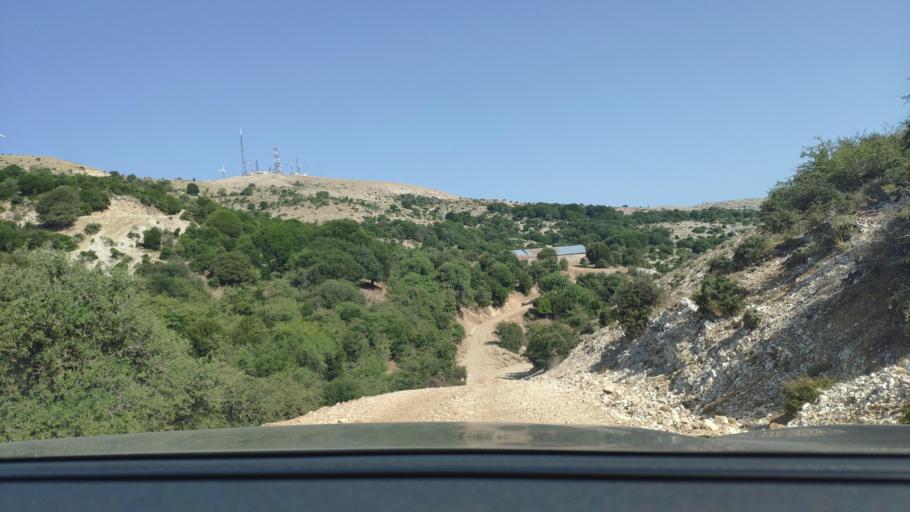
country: GR
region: West Greece
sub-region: Nomos Aitolias kai Akarnanias
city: Monastirakion
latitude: 38.8005
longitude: 20.9971
